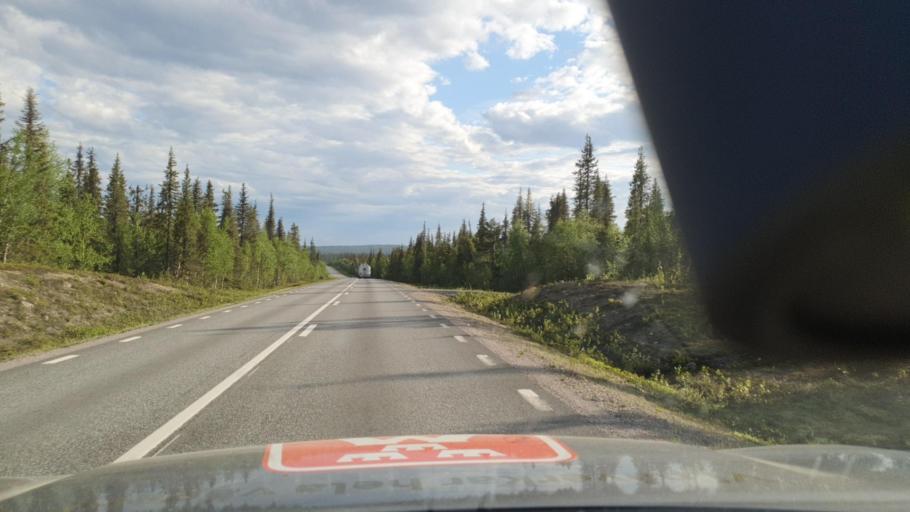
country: SE
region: Norrbotten
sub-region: Gallivare Kommun
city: Malmberget
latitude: 67.2724
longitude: 21.0423
